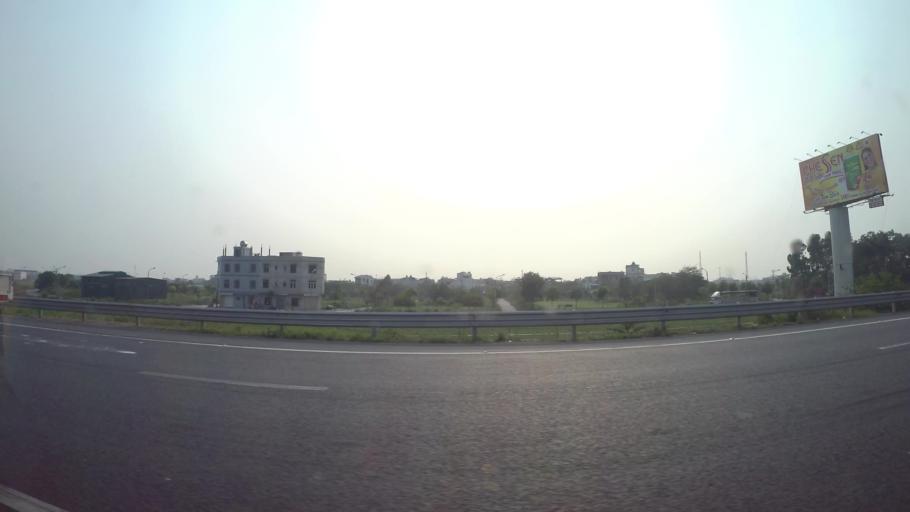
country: VN
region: Ha Noi
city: Van Dien
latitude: 20.9092
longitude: 105.8607
